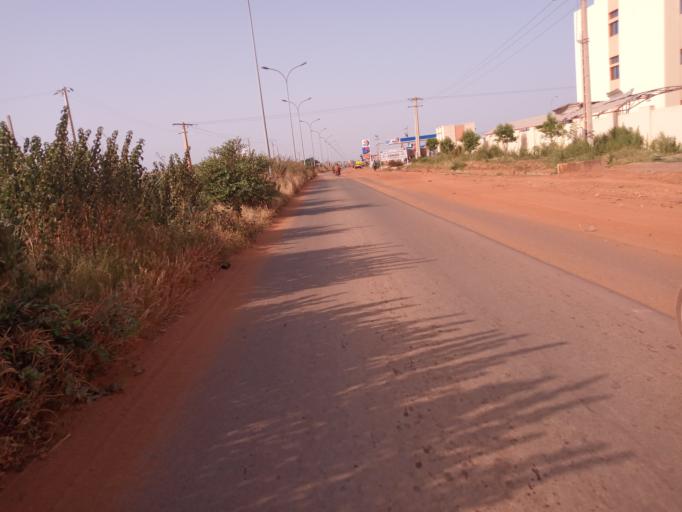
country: ML
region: Bamako
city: Bamako
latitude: 12.4880
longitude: -8.0565
